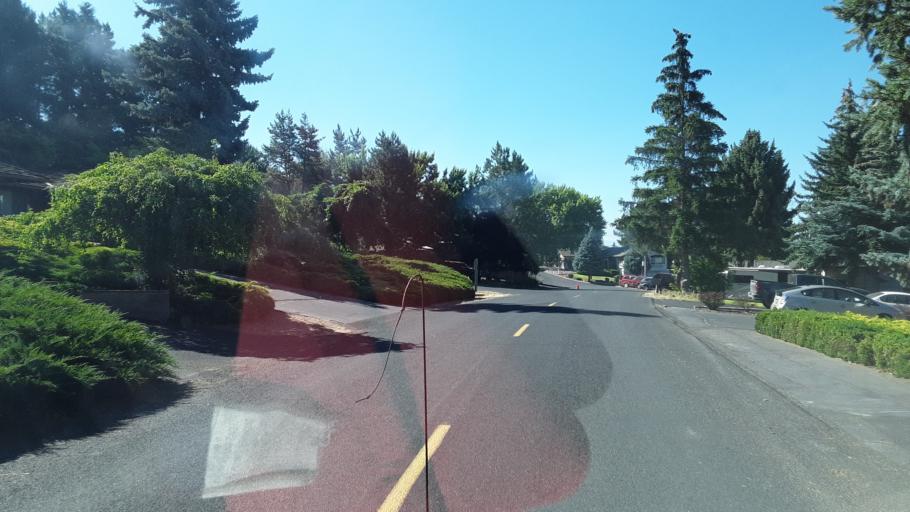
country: US
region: Oregon
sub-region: Klamath County
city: Altamont
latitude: 42.2162
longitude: -121.7078
